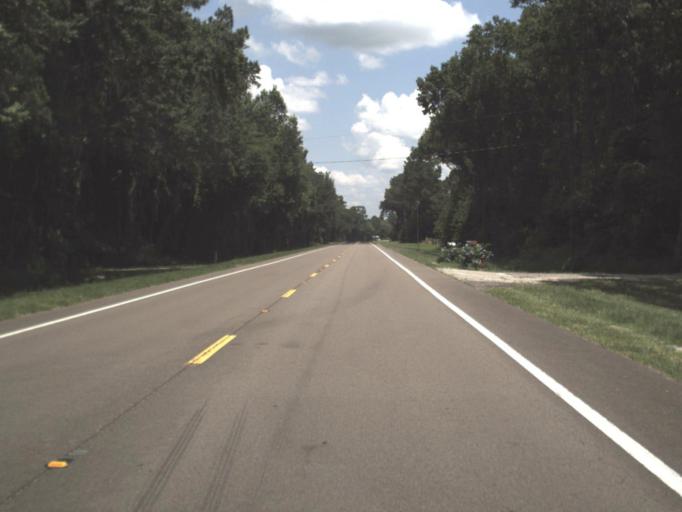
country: US
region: Florida
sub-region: Alachua County
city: Alachua
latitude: 29.7927
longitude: -82.3814
